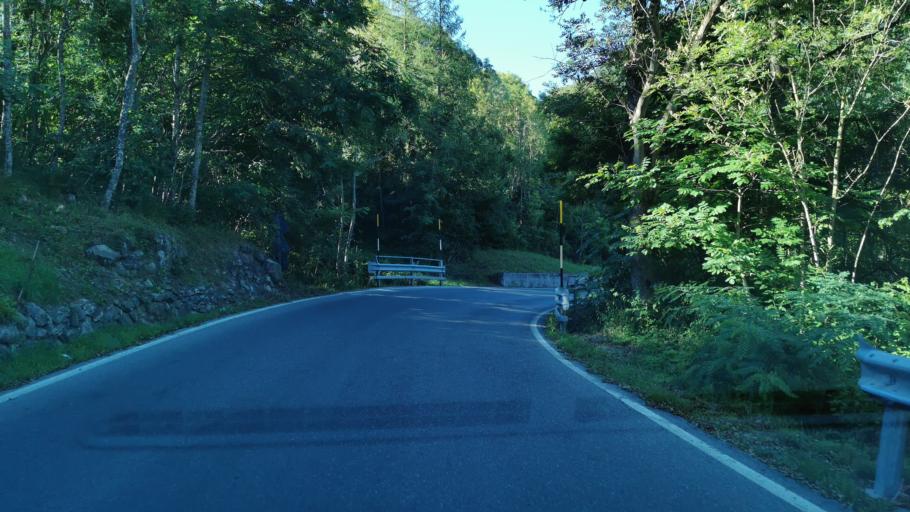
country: IT
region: Piedmont
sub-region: Provincia di Cuneo
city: Entracque
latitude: 44.2526
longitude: 7.3886
